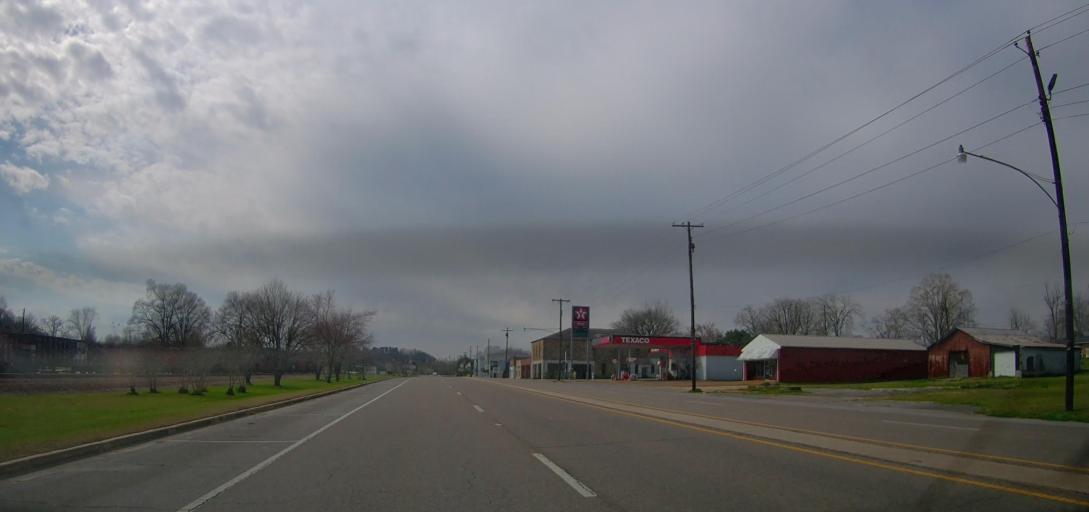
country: US
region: Alabama
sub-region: Walker County
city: Carbon Hill
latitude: 33.8879
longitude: -87.5272
